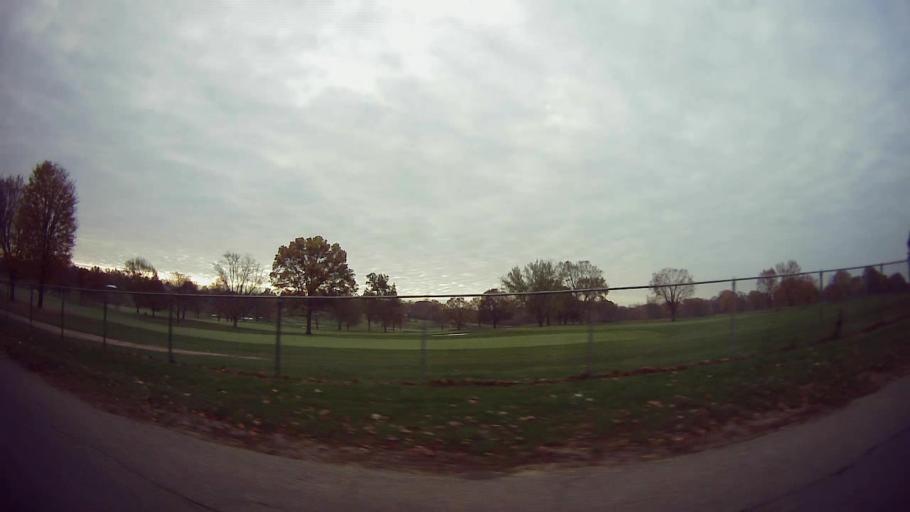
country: US
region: Michigan
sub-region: Oakland County
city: Beverly Hills
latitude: 42.5358
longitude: -83.2389
